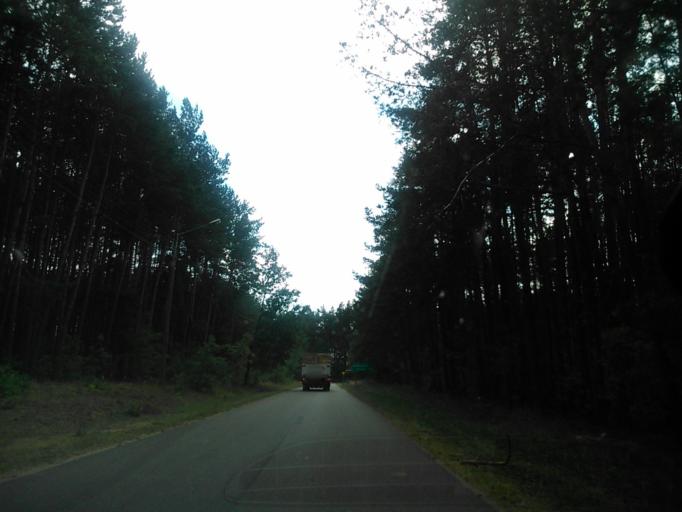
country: PL
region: Masovian Voivodeship
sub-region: Powiat ostrolecki
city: Czarnia
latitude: 53.3577
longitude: 21.1938
